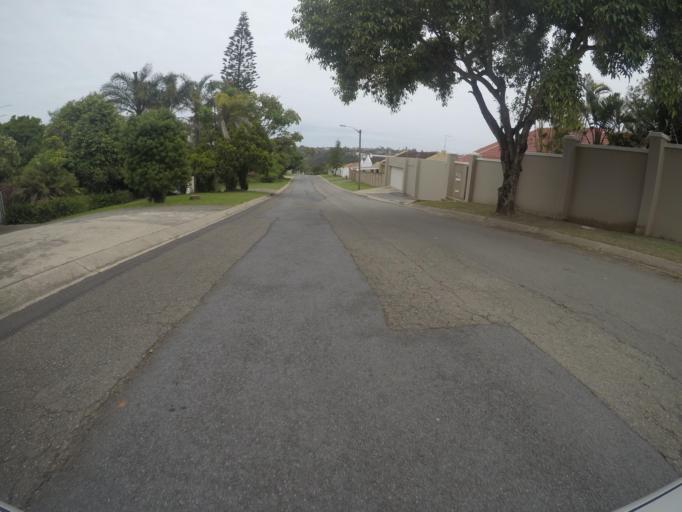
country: ZA
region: Eastern Cape
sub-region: Buffalo City Metropolitan Municipality
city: East London
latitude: -32.9784
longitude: 27.9390
